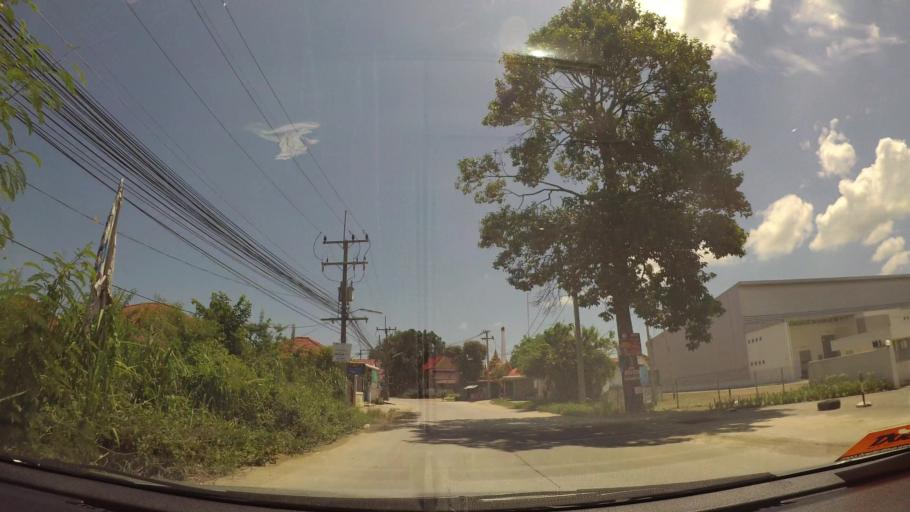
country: TH
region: Chon Buri
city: Si Racha
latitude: 13.1282
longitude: 100.9536
